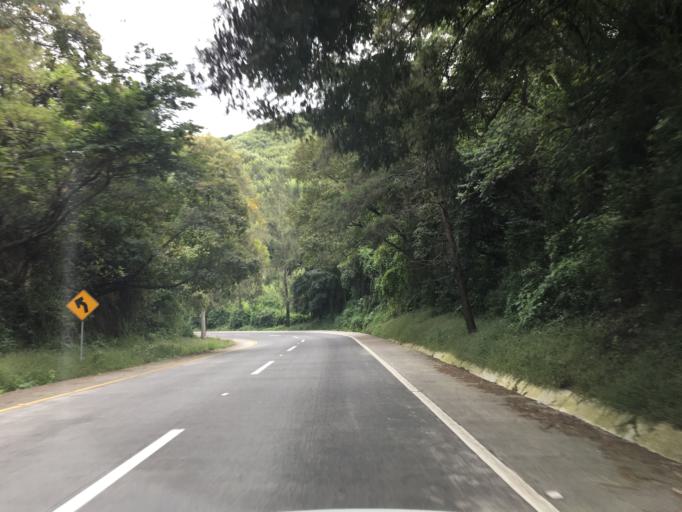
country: GT
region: Sacatepequez
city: Antigua Guatemala
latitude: 14.5585
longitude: -90.7048
